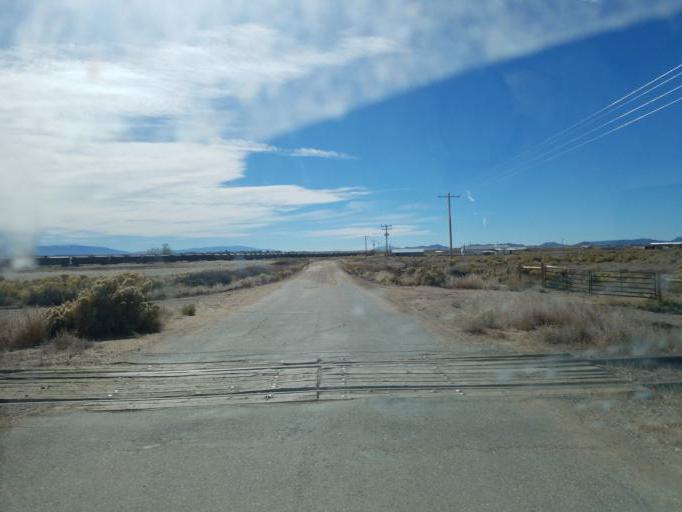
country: US
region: Colorado
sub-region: Costilla County
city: San Luis
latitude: 37.4352
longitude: -105.5235
